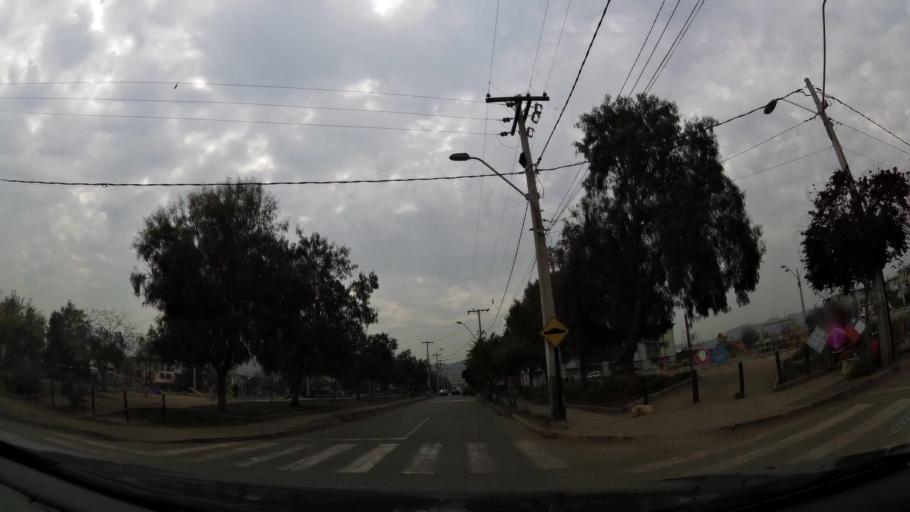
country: CL
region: Santiago Metropolitan
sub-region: Provincia de Chacabuco
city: Chicureo Abajo
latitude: -33.1890
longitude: -70.6675
